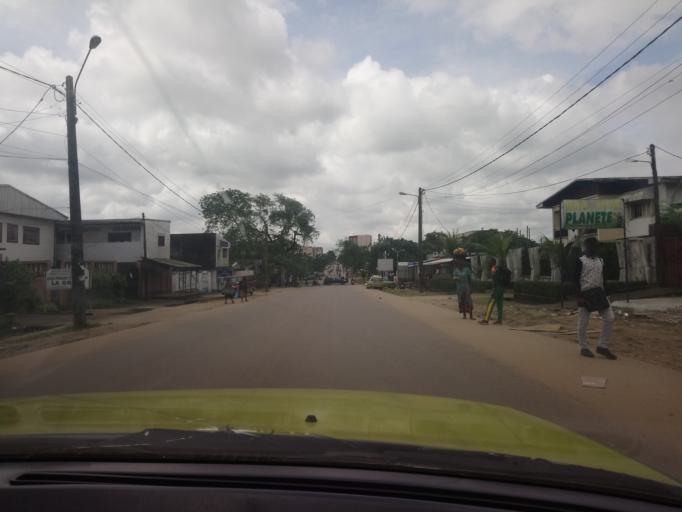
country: CM
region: Littoral
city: Douala
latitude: 4.0936
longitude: 9.7410
